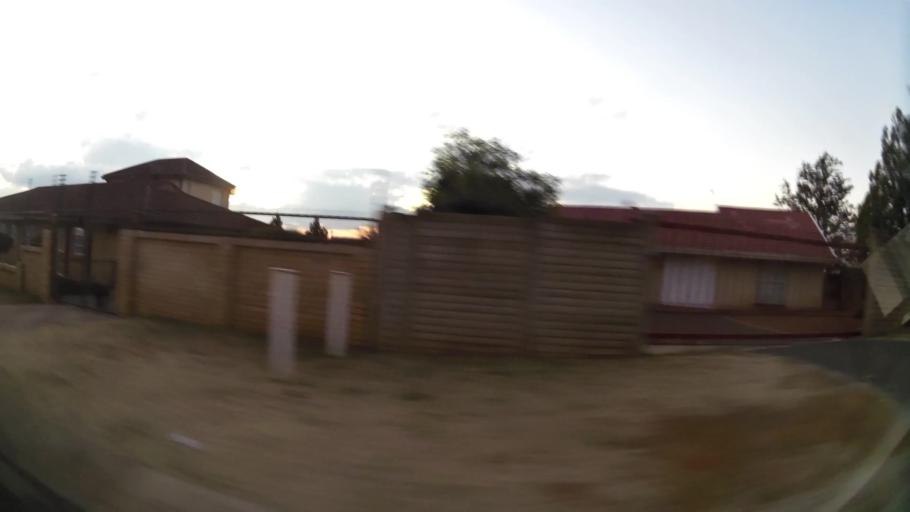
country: ZA
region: Orange Free State
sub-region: Mangaung Metropolitan Municipality
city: Bloemfontein
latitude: -29.1581
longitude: 26.1935
